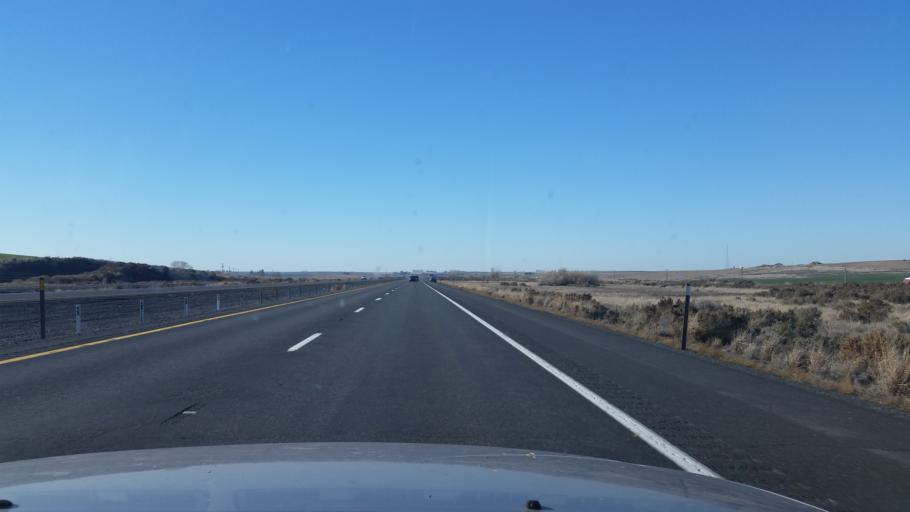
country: US
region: Washington
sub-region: Grant County
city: Warden
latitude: 47.0852
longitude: -119.0060
